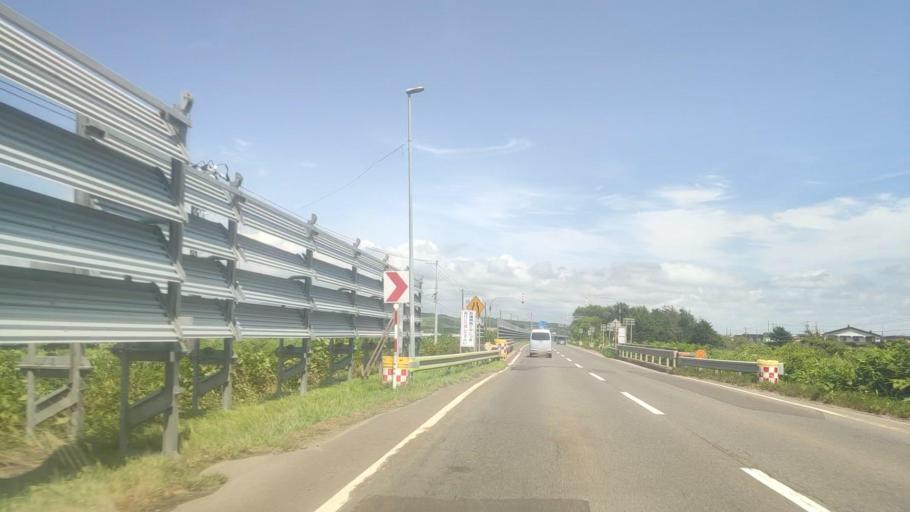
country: JP
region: Hokkaido
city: Nanae
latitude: 42.3030
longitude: 140.2720
